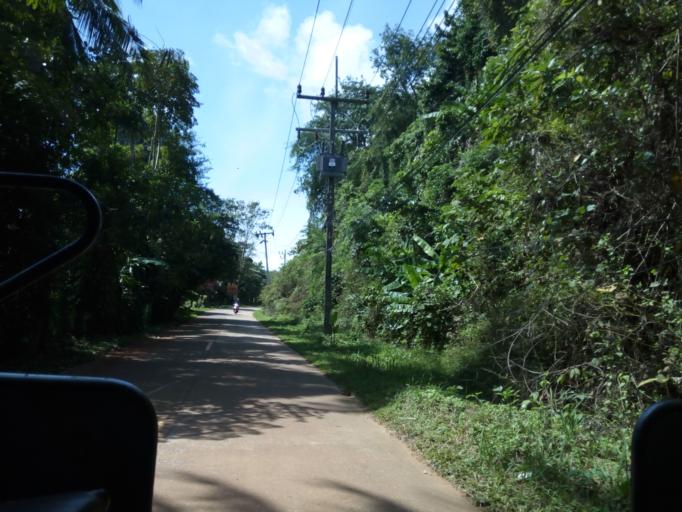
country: TH
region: Phangnga
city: Ko Yao
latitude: 8.1288
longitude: 98.6214
